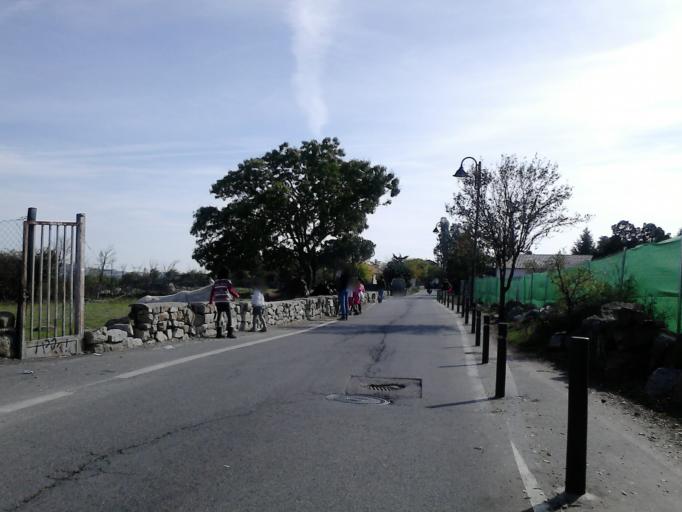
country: ES
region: Madrid
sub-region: Provincia de Madrid
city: Galapagar
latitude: 40.5779
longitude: -3.9980
